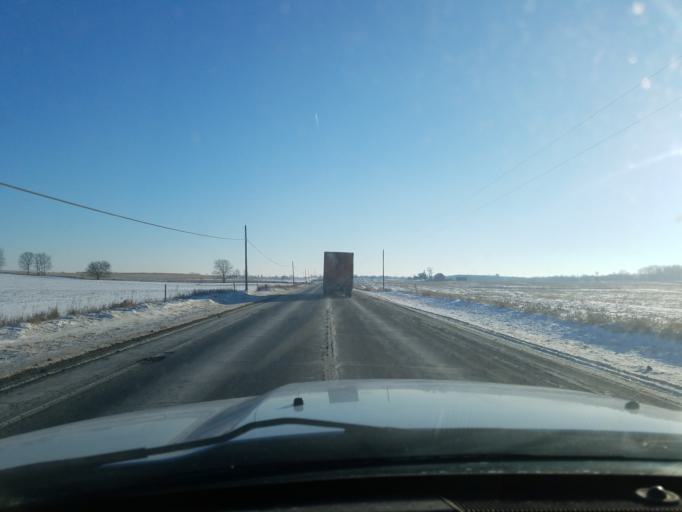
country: US
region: Indiana
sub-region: Noble County
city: Rome City
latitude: 41.4525
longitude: -85.3310
